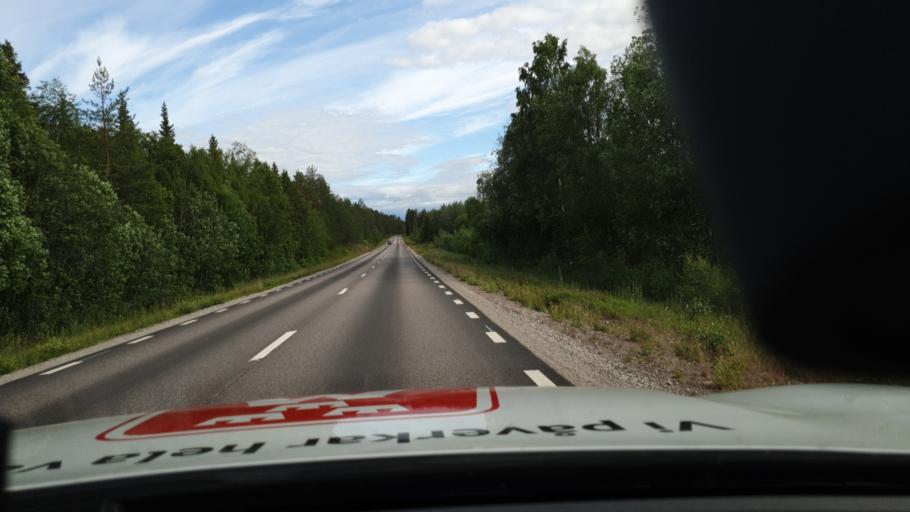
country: SE
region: Norrbotten
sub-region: Overkalix Kommun
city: OEverkalix
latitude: 66.4019
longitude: 22.8096
